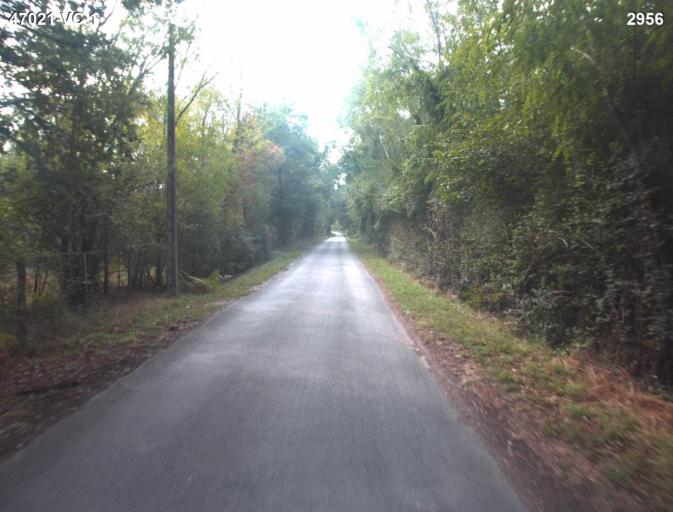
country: FR
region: Aquitaine
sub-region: Departement du Lot-et-Garonne
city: Barbaste
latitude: 44.1417
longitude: 0.2935
